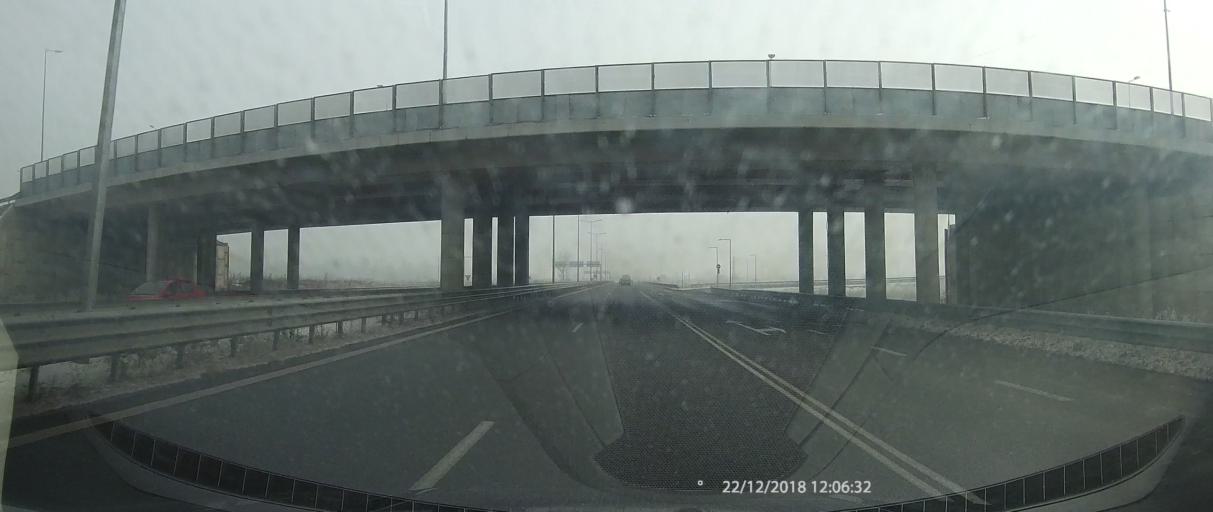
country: BG
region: Sofia-Capital
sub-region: Stolichna Obshtina
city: Sofia
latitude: 42.7537
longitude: 23.3414
